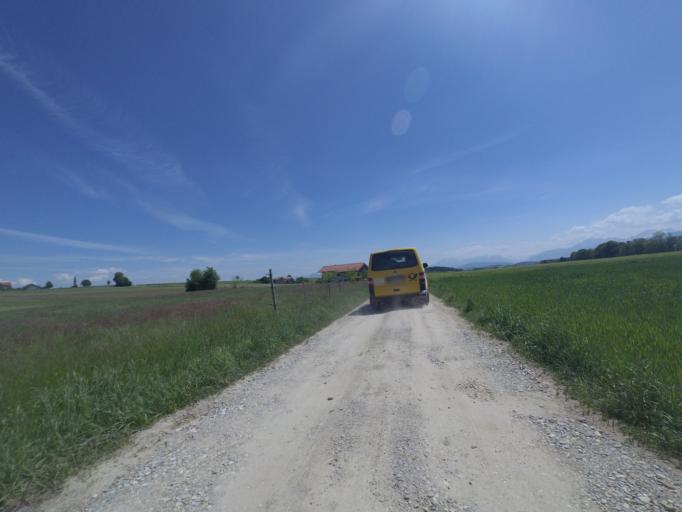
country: DE
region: Bavaria
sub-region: Upper Bavaria
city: Petting
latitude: 47.9403
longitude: 12.7968
